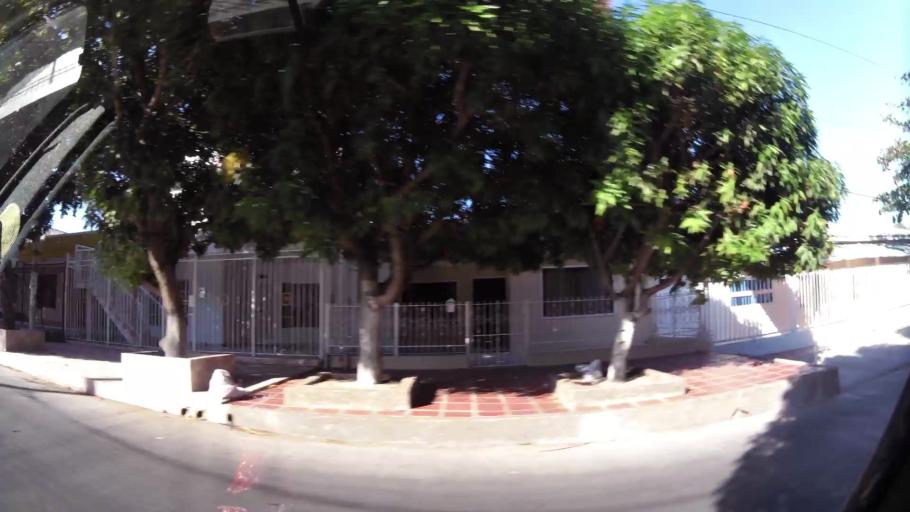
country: CO
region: Atlantico
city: Barranquilla
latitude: 10.9626
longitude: -74.7880
